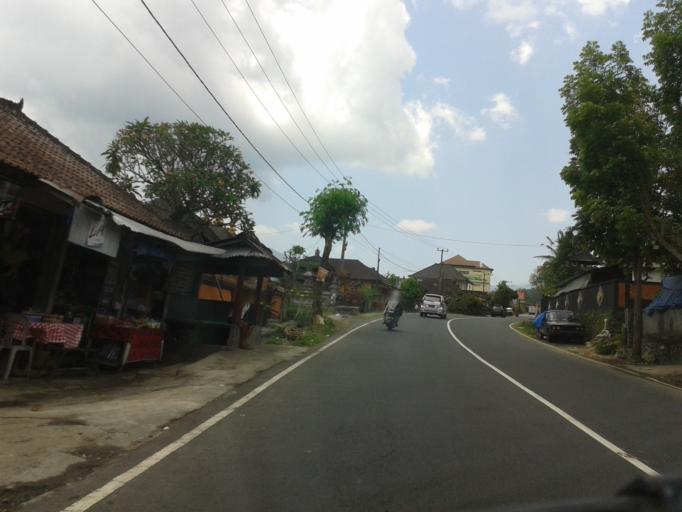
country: ID
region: Bali
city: Peneng
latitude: -8.3579
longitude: 115.1901
